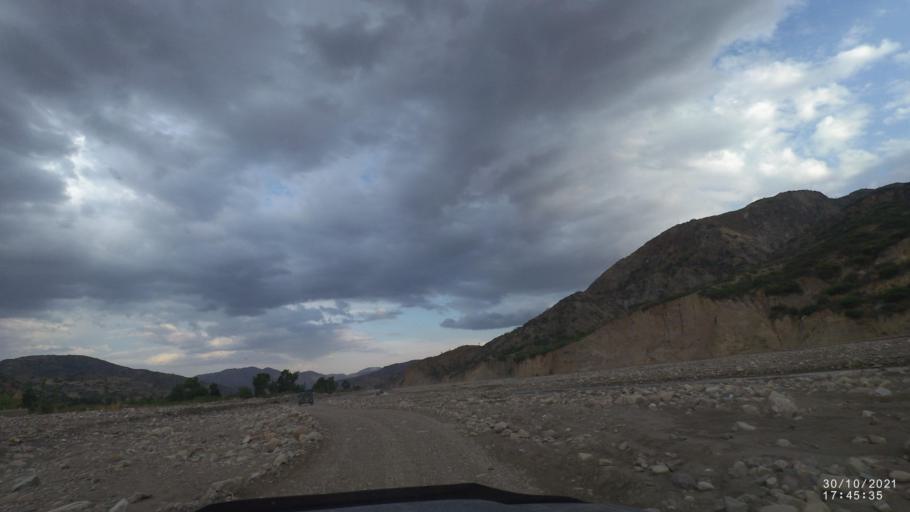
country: BO
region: Cochabamba
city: Sipe Sipe
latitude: -17.5317
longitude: -66.5304
